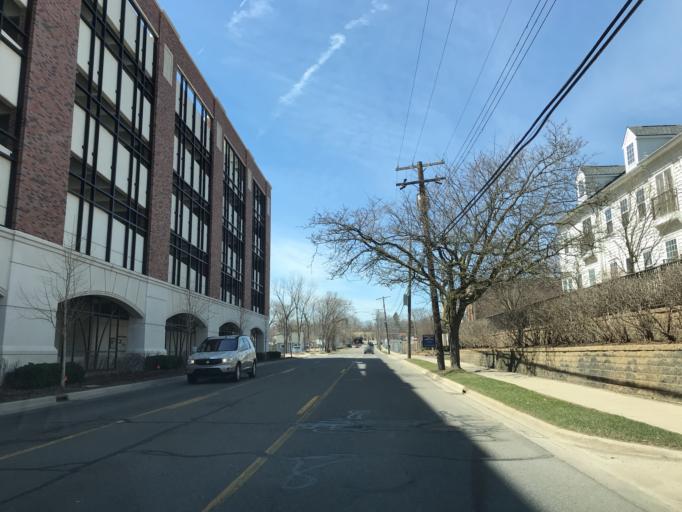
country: US
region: Michigan
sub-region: Washtenaw County
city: Ann Arbor
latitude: 42.2882
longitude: -83.7346
